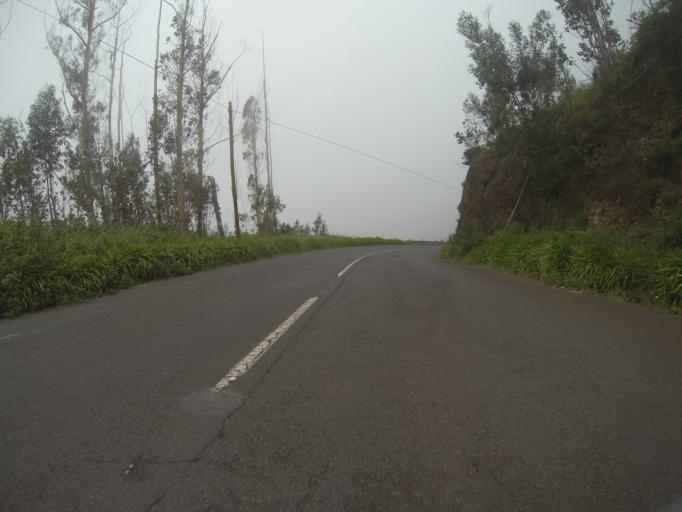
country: PT
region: Madeira
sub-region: Funchal
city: Nossa Senhora do Monte
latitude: 32.6891
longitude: -16.9016
